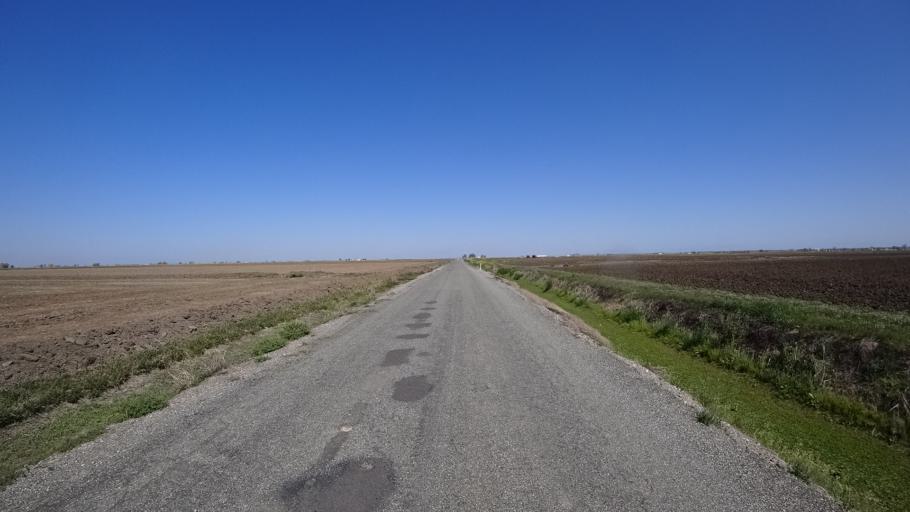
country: US
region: California
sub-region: Glenn County
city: Willows
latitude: 39.4318
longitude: -122.0649
